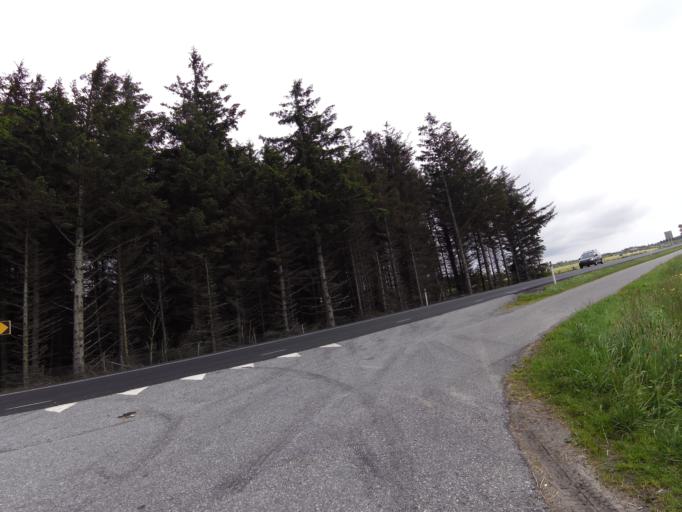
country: NO
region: Rogaland
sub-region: Ha
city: Naerbo
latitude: 58.6529
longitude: 5.5998
